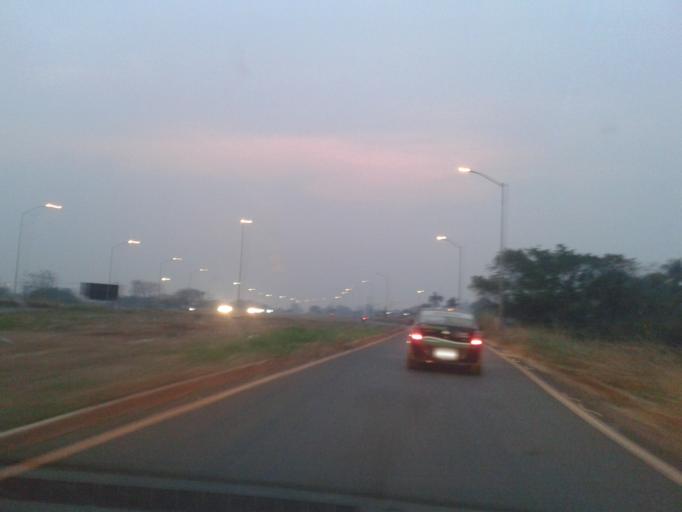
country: BR
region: Minas Gerais
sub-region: Ituiutaba
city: Ituiutaba
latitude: -18.9662
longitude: -49.4881
